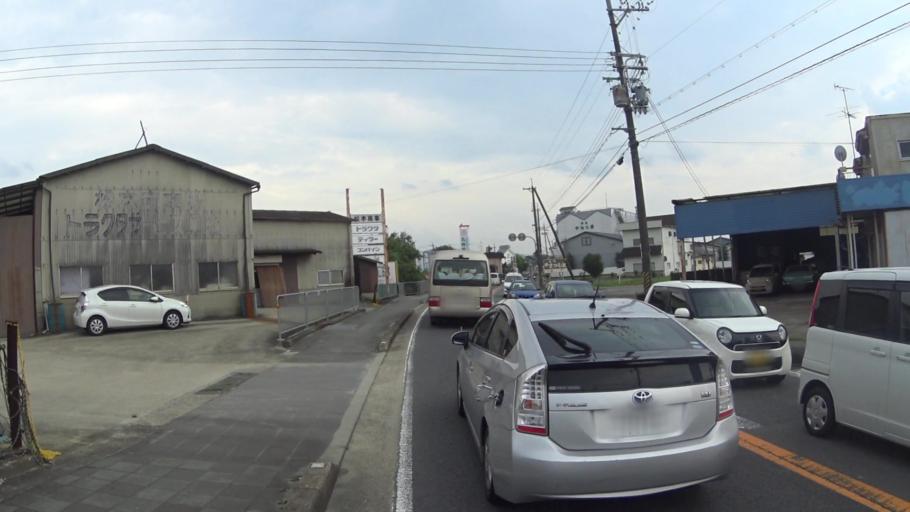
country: JP
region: Nara
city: Nara-shi
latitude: 34.7490
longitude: 135.8193
